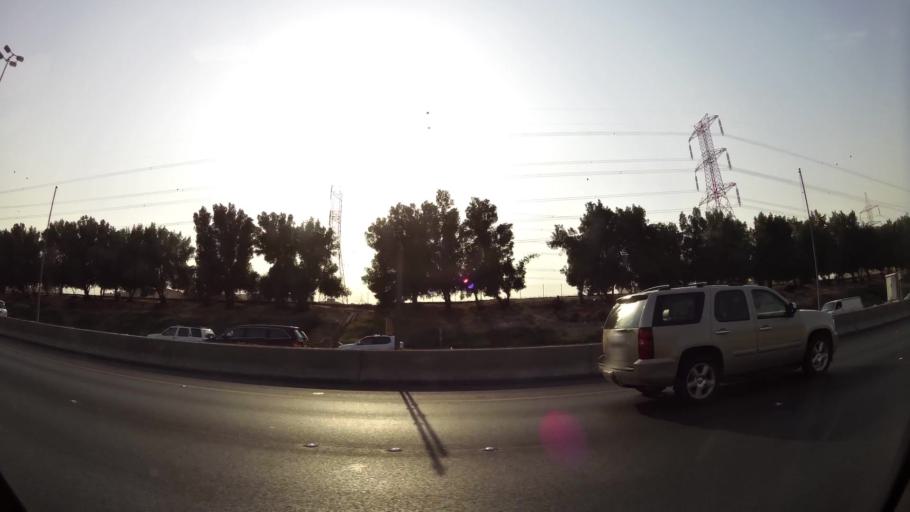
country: KW
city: Bayan
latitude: 29.3001
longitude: 48.0252
